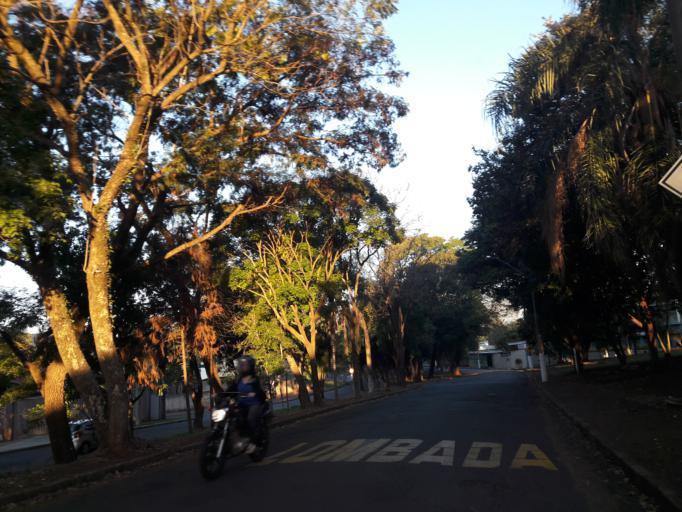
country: BR
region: Sao Paulo
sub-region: Moji-Guacu
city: Mogi-Gaucu
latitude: -22.3660
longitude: -46.9366
